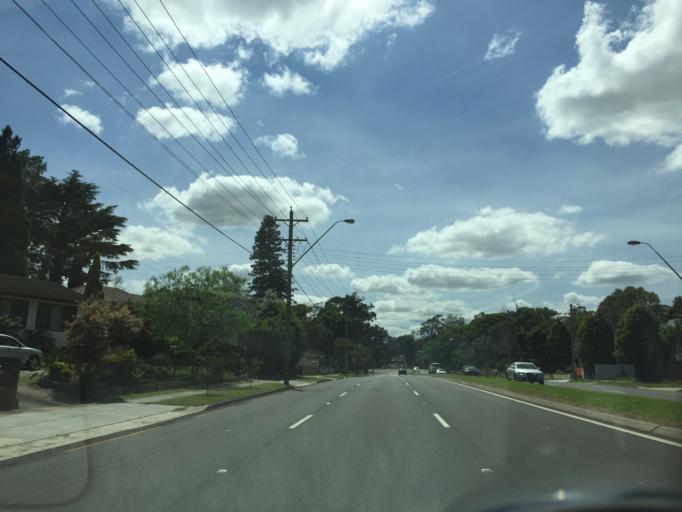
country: AU
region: New South Wales
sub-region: Parramatta
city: Telopea
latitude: -33.8041
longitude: 151.0290
